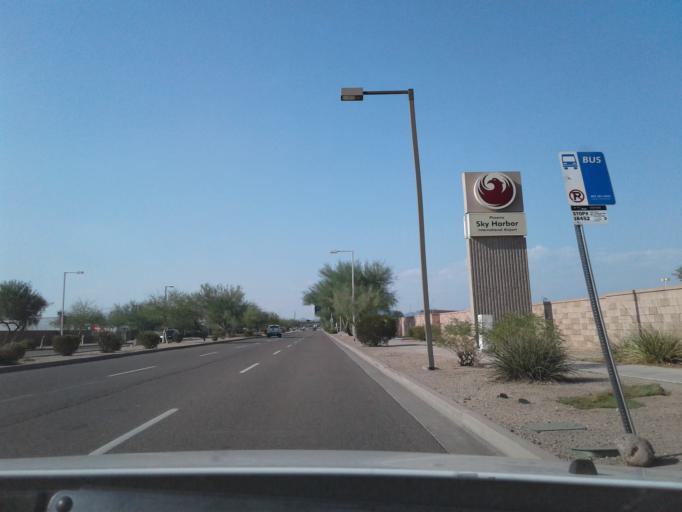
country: US
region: Arizona
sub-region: Maricopa County
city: Phoenix
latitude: 33.4319
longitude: -112.0346
